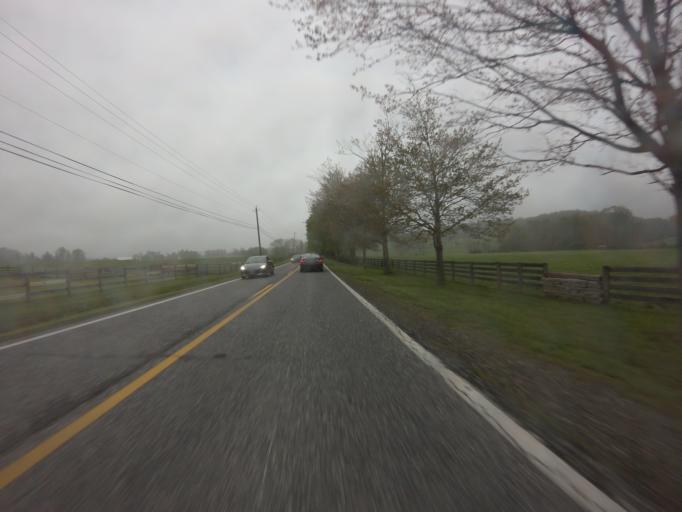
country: US
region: Maryland
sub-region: Baltimore County
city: Owings Mills
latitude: 39.4914
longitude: -76.7473
